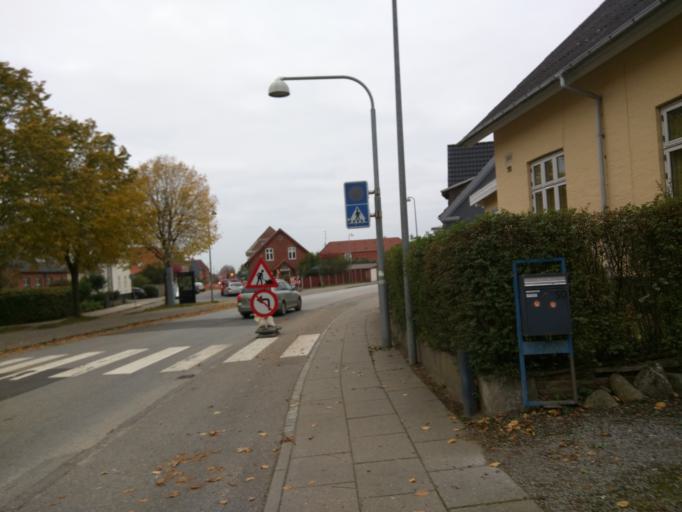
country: DK
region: Central Jutland
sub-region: Viborg Kommune
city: Viborg
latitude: 56.4541
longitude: 9.3974
